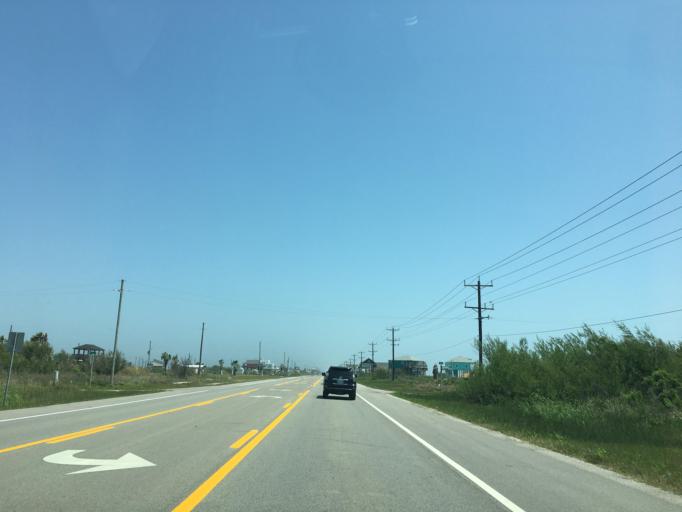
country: US
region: Texas
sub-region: Galveston County
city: Bolivar Peninsula
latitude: 29.5095
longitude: -94.4972
